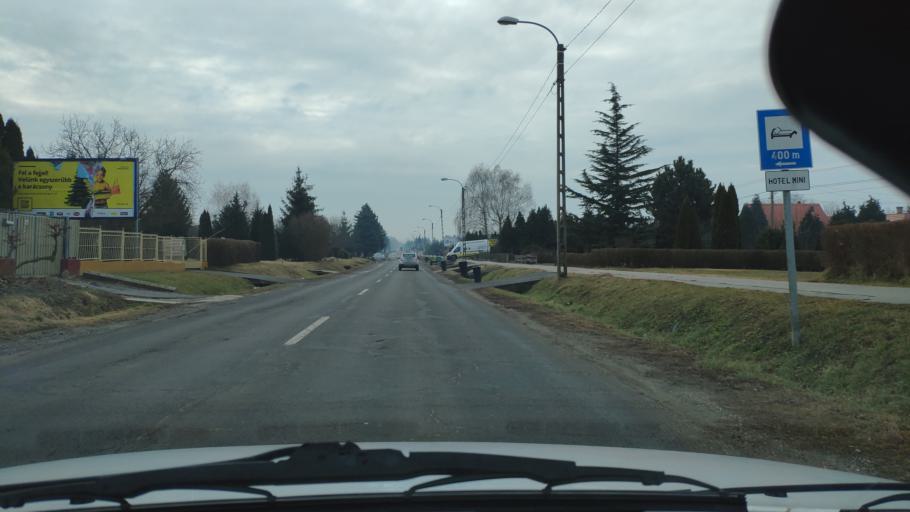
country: HU
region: Zala
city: Nagykanizsa
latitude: 46.4912
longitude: 16.9846
